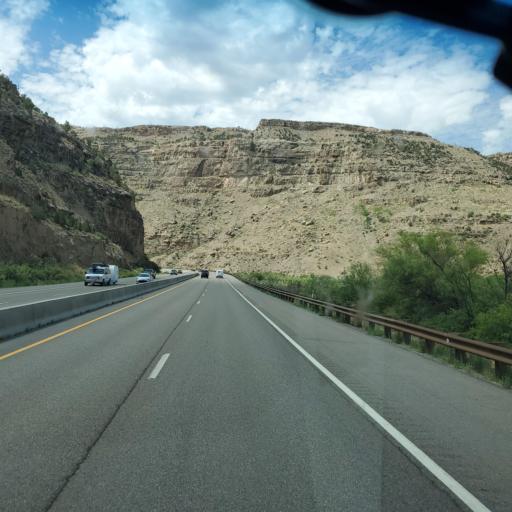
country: US
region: Colorado
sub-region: Mesa County
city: Palisade
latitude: 39.2370
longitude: -108.2707
